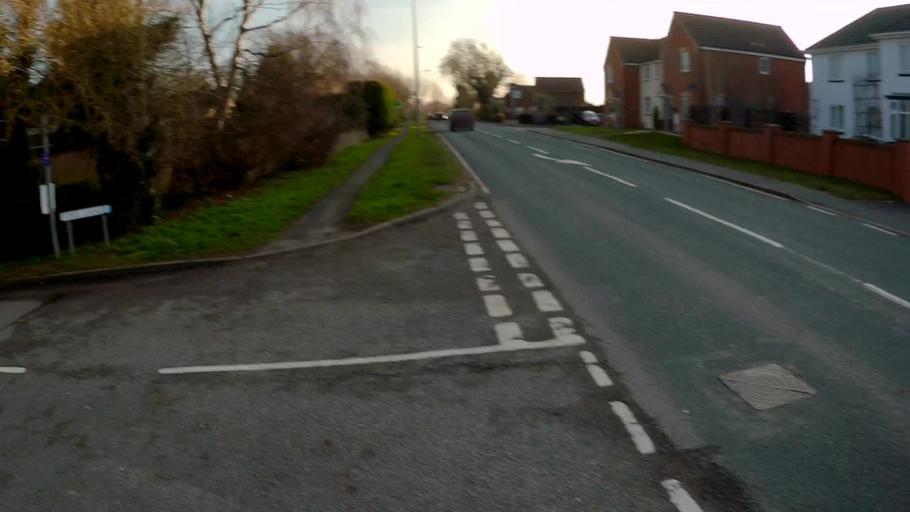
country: GB
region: England
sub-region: Lincolnshire
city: Bourne
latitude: 52.8015
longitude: -0.3797
